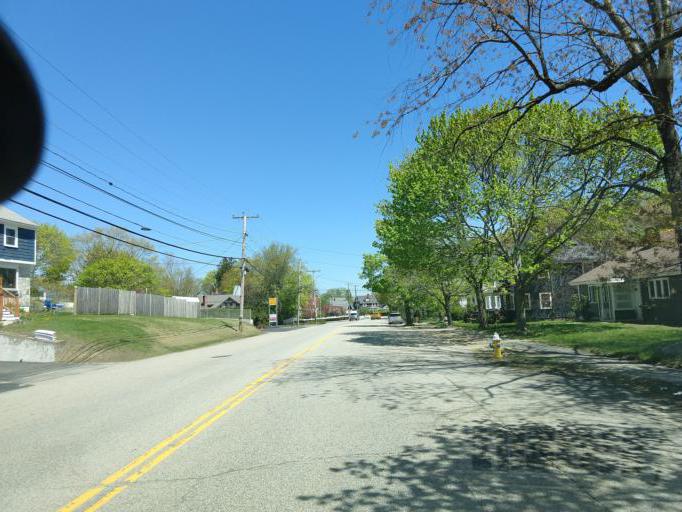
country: US
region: New Hampshire
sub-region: Rockingham County
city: Portsmouth
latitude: 43.0637
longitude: -70.7677
